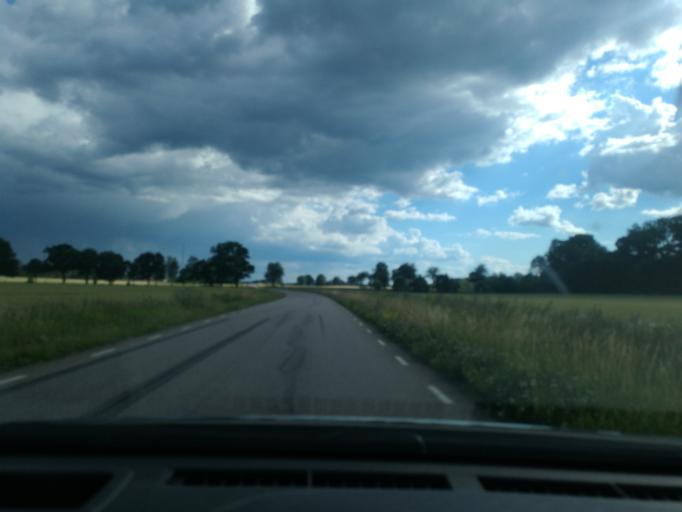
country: SE
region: Soedermanland
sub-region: Eskilstuna Kommun
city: Arla
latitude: 59.4450
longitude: 16.7207
